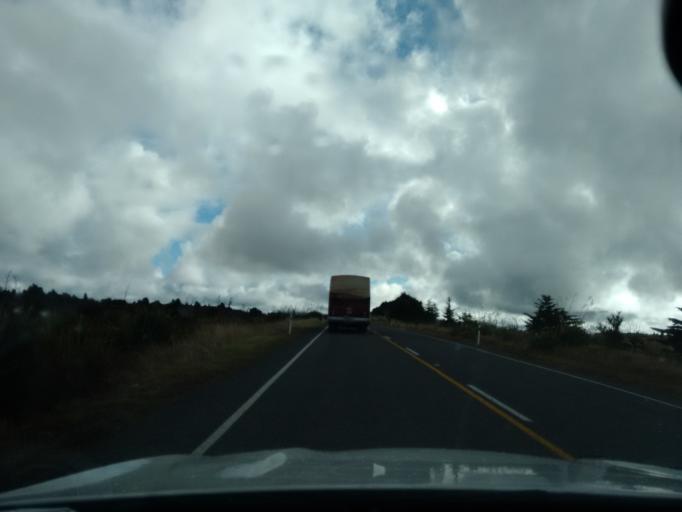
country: NZ
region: Manawatu-Wanganui
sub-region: Ruapehu District
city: Waiouru
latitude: -39.1788
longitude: 175.4615
